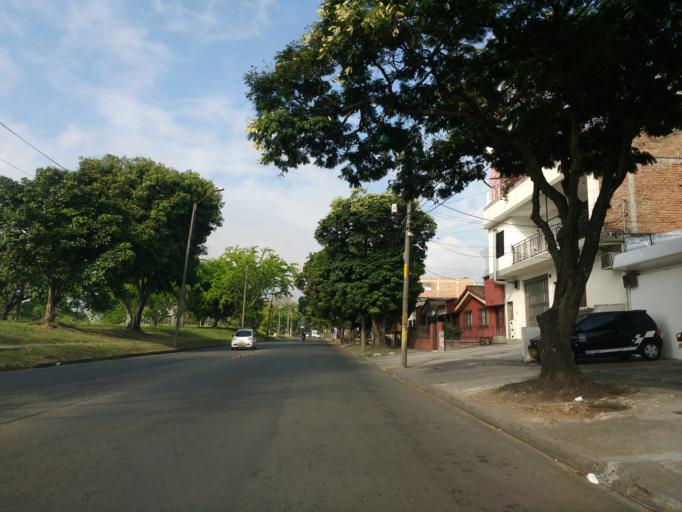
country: CO
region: Valle del Cauca
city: Cali
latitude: 3.4768
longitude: -76.5131
